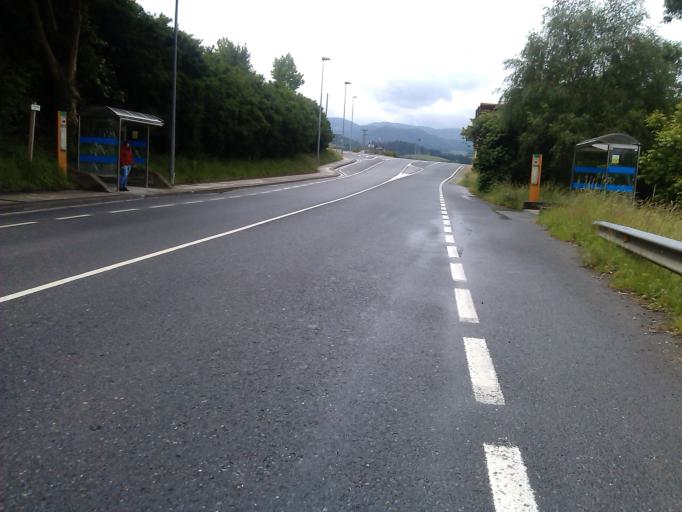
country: ES
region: Basque Country
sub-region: Provincia de Guipuzcoa
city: Urnieta
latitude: 43.2365
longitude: -1.9989
